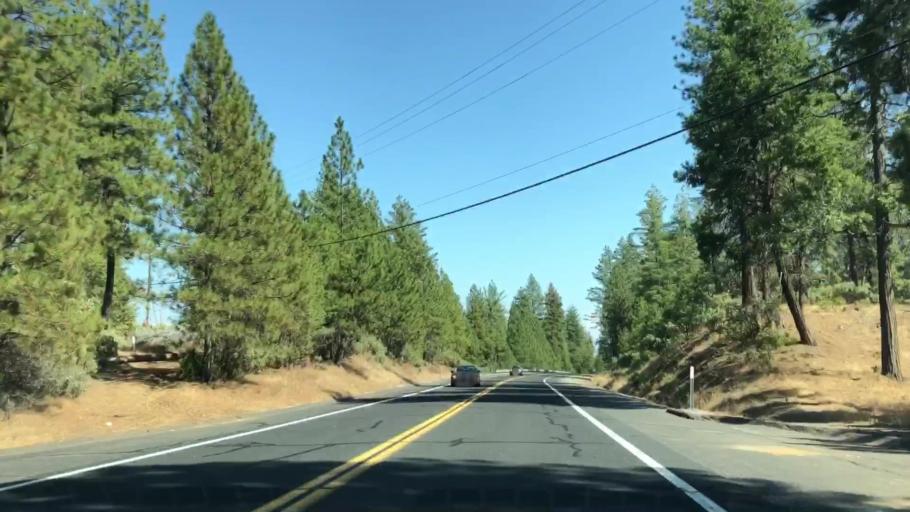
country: US
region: California
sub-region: Tuolumne County
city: Tuolumne City
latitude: 37.8277
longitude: -120.1803
